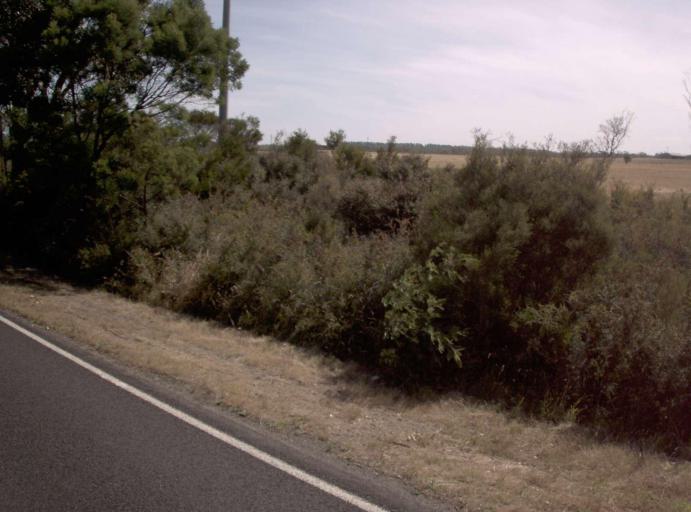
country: AU
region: Victoria
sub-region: Wellington
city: Sale
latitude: -38.3482
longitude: 147.1722
